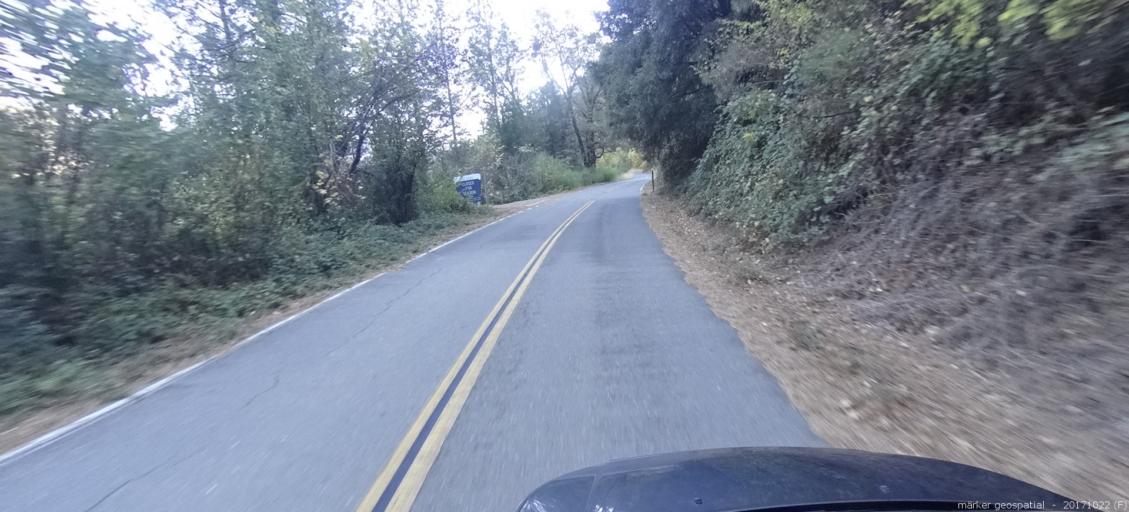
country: US
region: California
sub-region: Shasta County
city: Shasta Lake
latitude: 40.9268
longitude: -122.2489
